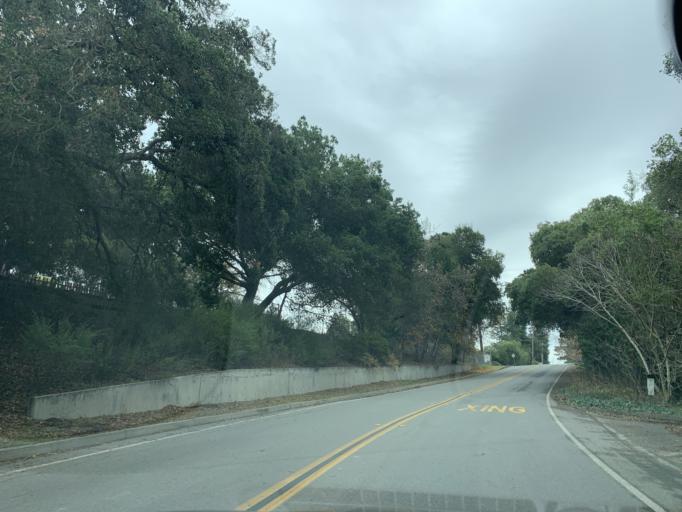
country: US
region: California
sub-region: Santa Clara County
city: Loyola
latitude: 37.3431
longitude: -122.0963
